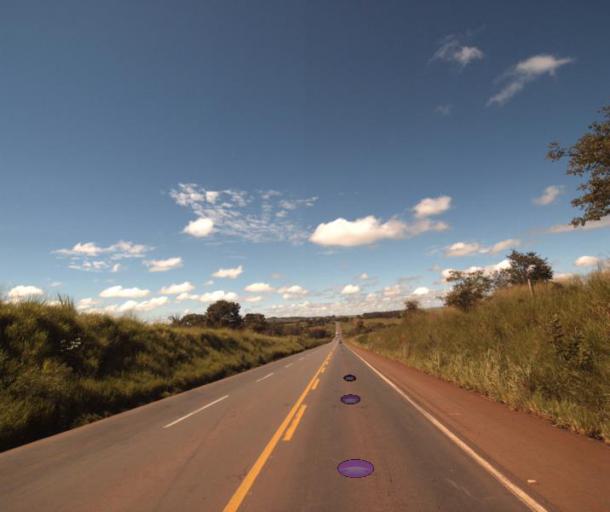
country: BR
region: Goias
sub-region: Rialma
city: Rialma
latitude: -15.3831
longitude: -49.5528
